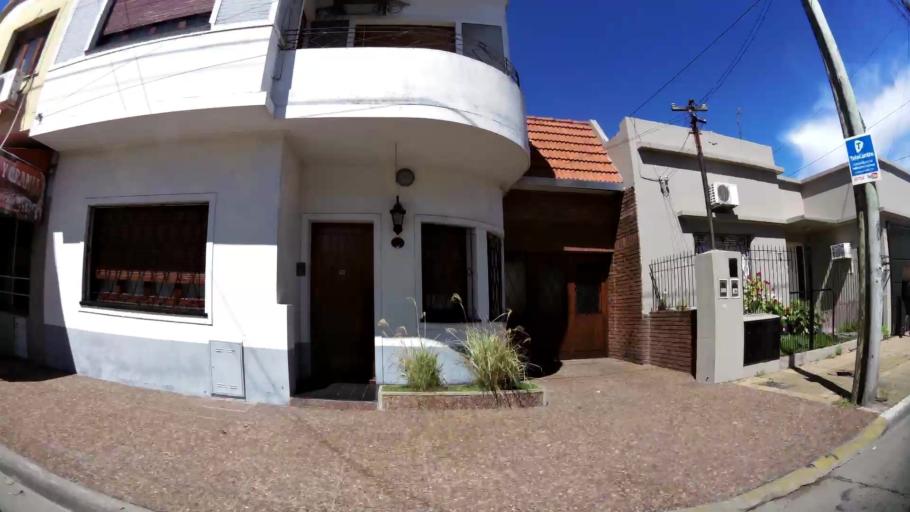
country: AR
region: Buenos Aires
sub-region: Partido de Quilmes
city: Quilmes
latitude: -34.7080
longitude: -58.2747
